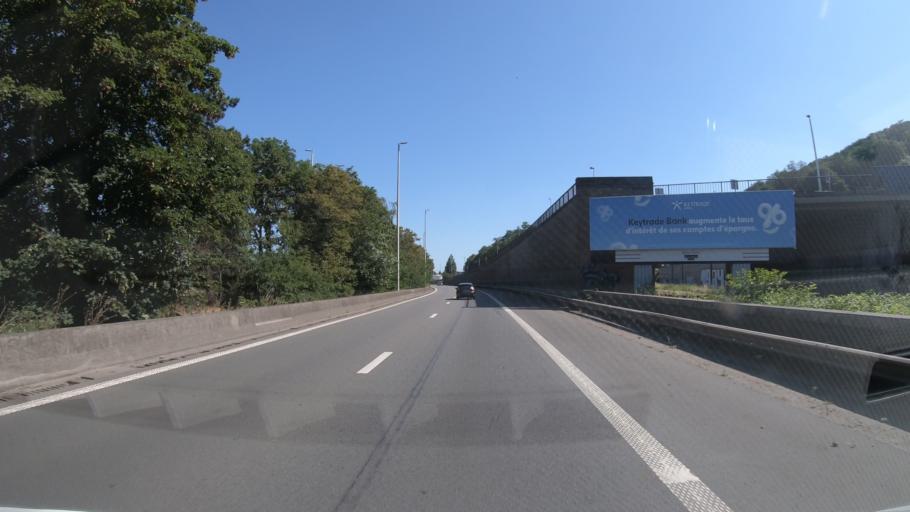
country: BE
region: Wallonia
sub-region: Province de Liege
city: Herstal
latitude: 50.6547
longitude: 5.6456
